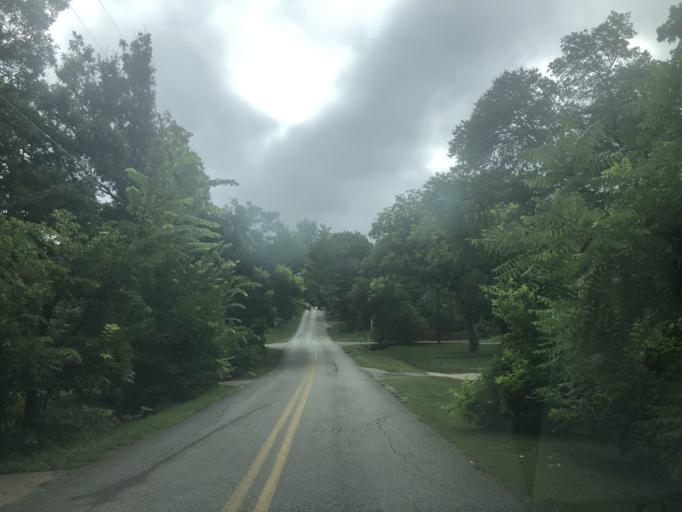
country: US
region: Texas
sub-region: Dallas County
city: Duncanville
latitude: 32.6736
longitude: -96.9233
